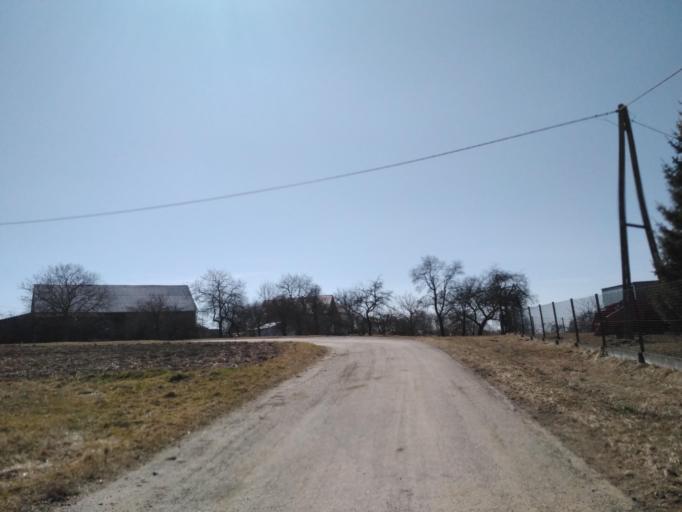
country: PL
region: Subcarpathian Voivodeship
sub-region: Powiat brzozowski
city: Jablonica Polska
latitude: 49.7406
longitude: 21.8938
